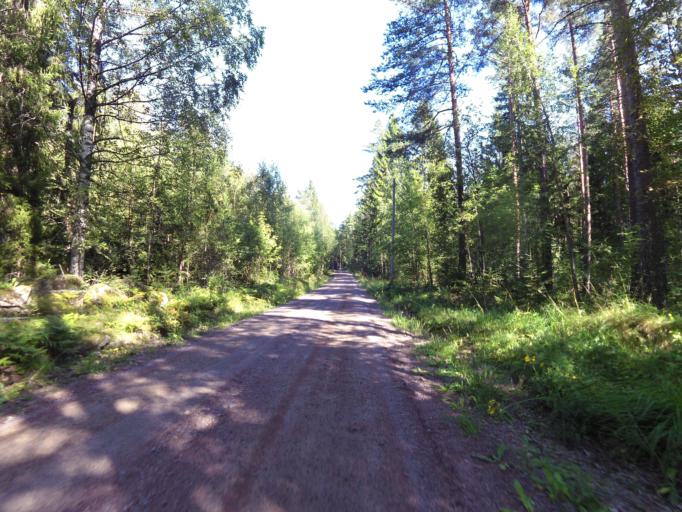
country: SE
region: Gaevleborg
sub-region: Hofors Kommun
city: Hofors
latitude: 60.5454
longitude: 16.4654
